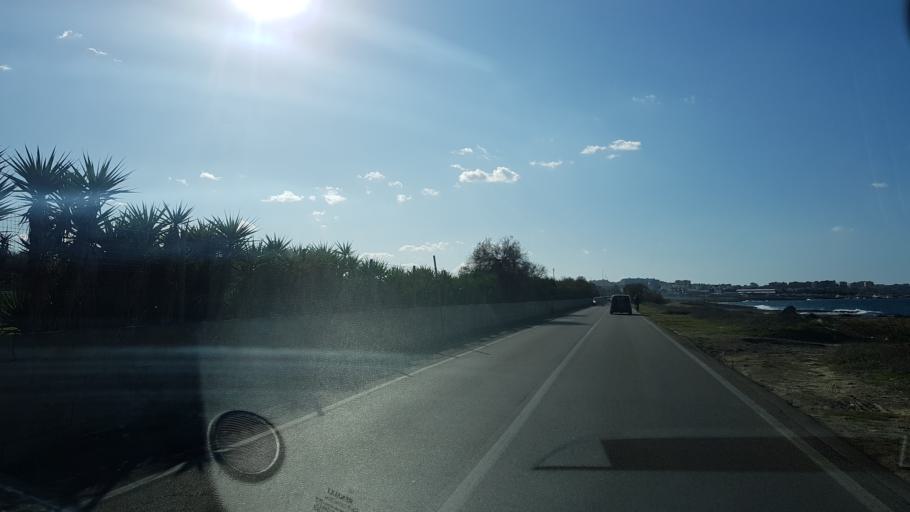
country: IT
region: Apulia
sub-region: Provincia di Lecce
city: Gallipoli
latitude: 40.0774
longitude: 18.0074
